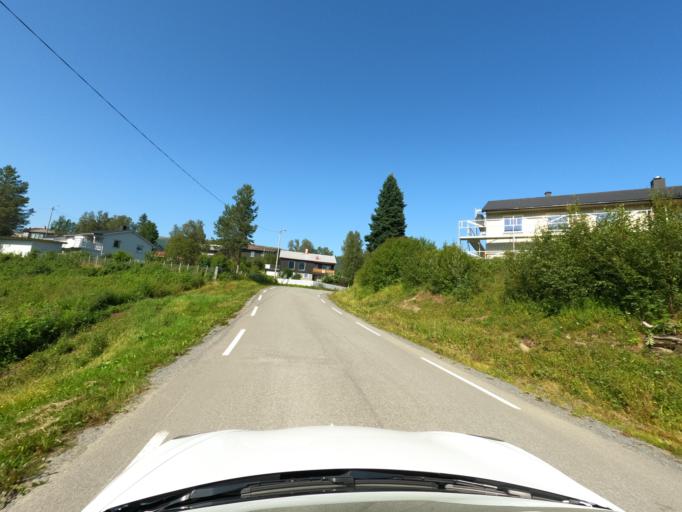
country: NO
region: Nordland
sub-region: Ballangen
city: Ballangen
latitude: 68.3428
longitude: 16.8210
